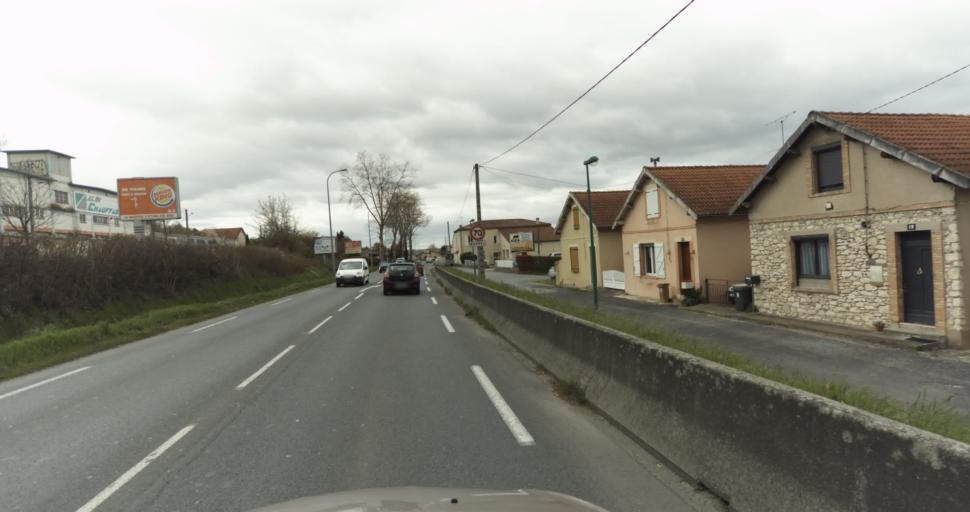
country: FR
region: Midi-Pyrenees
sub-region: Departement du Tarn
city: Puygouzon
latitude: 43.9036
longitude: 2.1432
